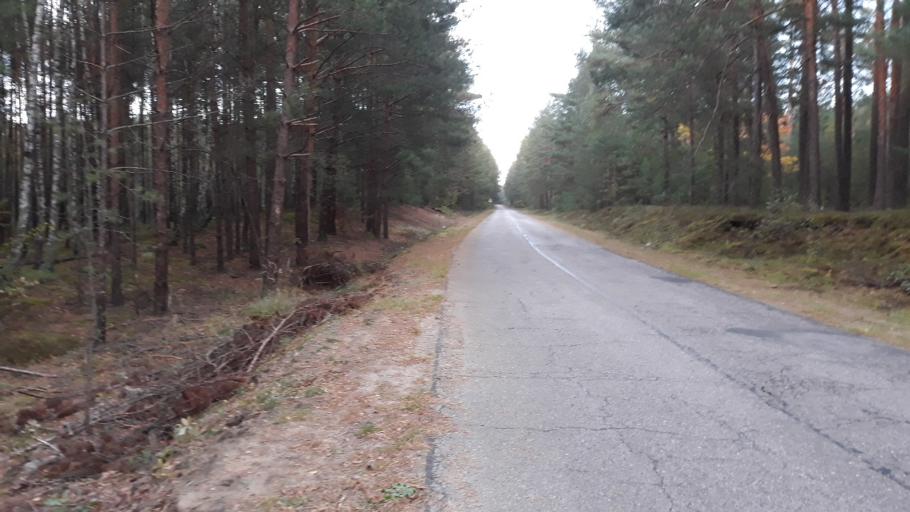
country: PL
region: Lublin Voivodeship
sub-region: Powiat janowski
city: Dzwola
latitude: 50.6457
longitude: 22.5848
